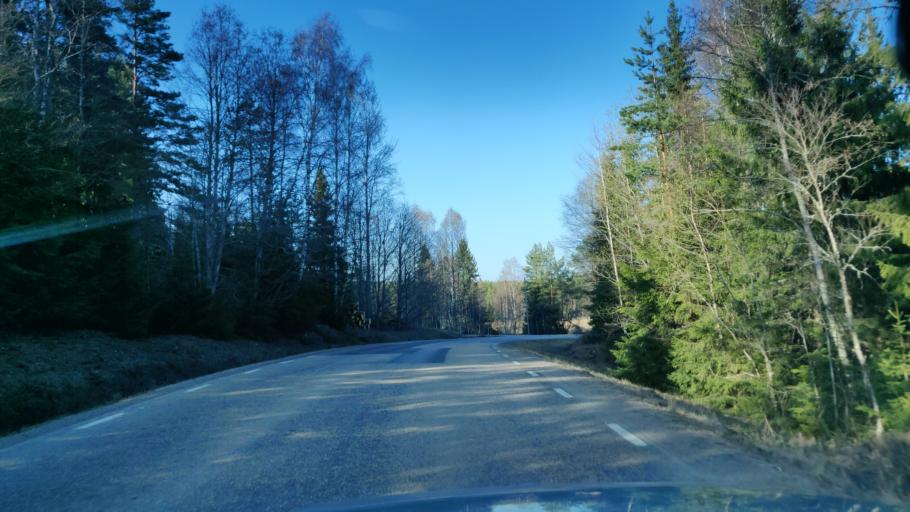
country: SE
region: Vaermland
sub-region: Sunne Kommun
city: Sunne
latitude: 59.9885
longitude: 13.2705
